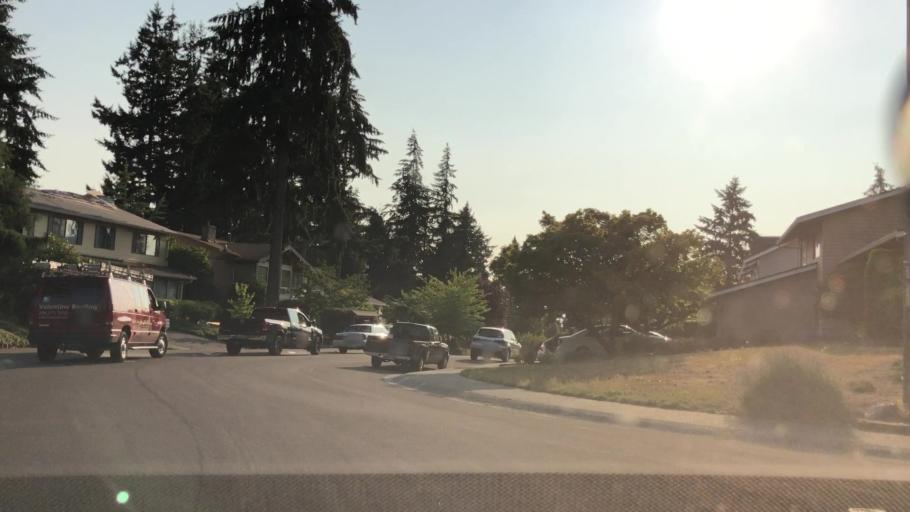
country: US
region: Washington
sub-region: King County
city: Kingsgate
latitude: 47.6983
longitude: -122.1679
